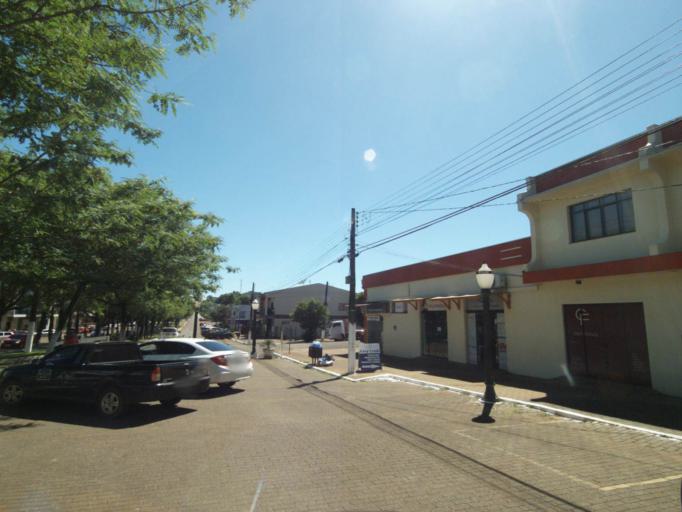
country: BR
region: Santa Catarina
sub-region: Sao Lourenco Do Oeste
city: Sao Lourenco dOeste
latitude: -26.2661
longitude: -52.7820
